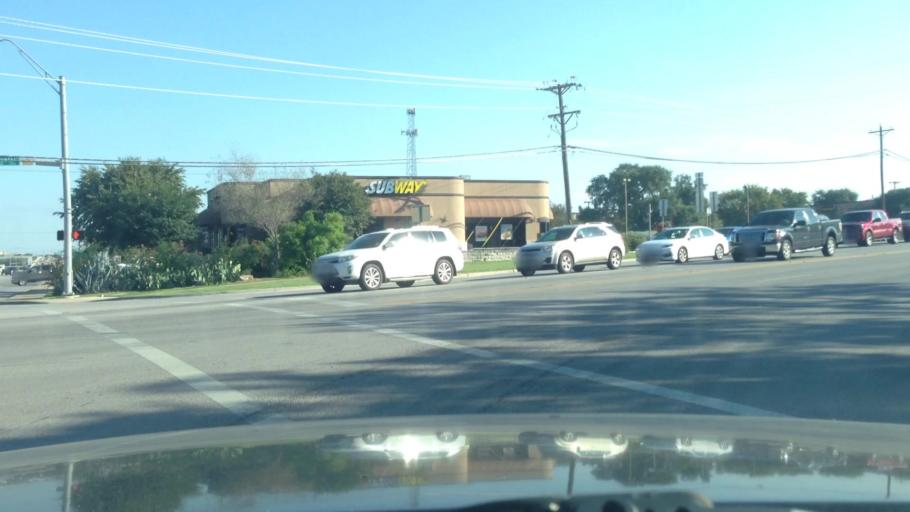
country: US
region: Texas
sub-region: Hays County
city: San Marcos
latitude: 29.8659
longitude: -97.9637
